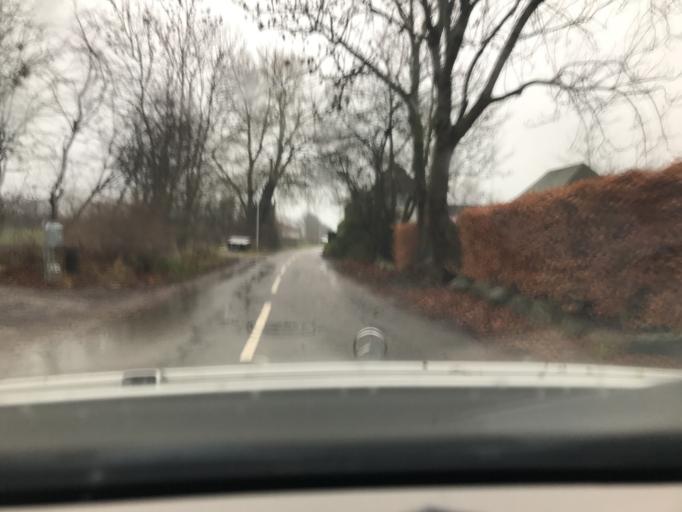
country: DK
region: South Denmark
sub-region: Sonderborg Kommune
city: Horuphav
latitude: 54.8927
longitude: 10.0307
